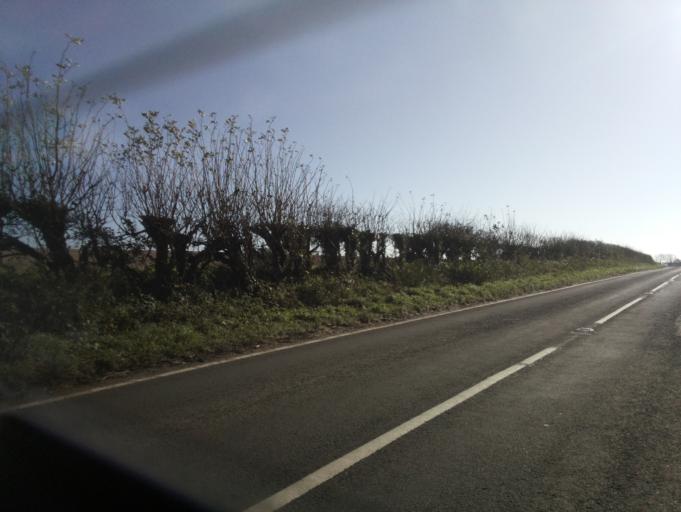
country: GB
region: England
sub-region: Dorset
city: Dorchester
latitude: 50.8302
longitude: -2.4665
